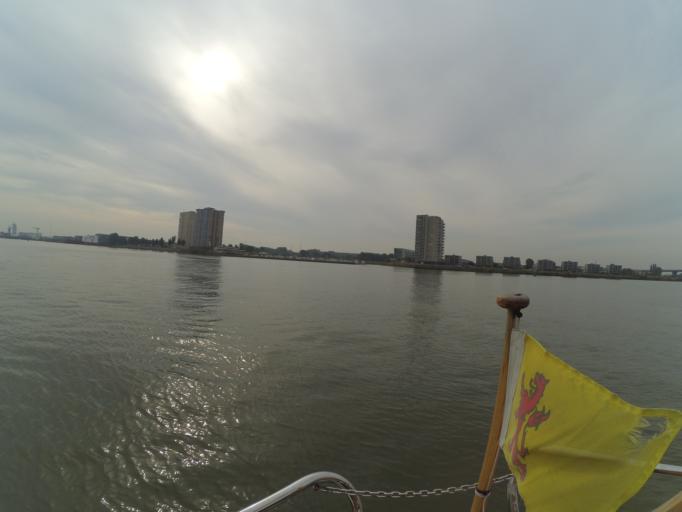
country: NL
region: South Holland
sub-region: Gemeente Capelle aan den IJssel
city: Capelle-West
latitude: 51.9058
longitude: 4.5555
